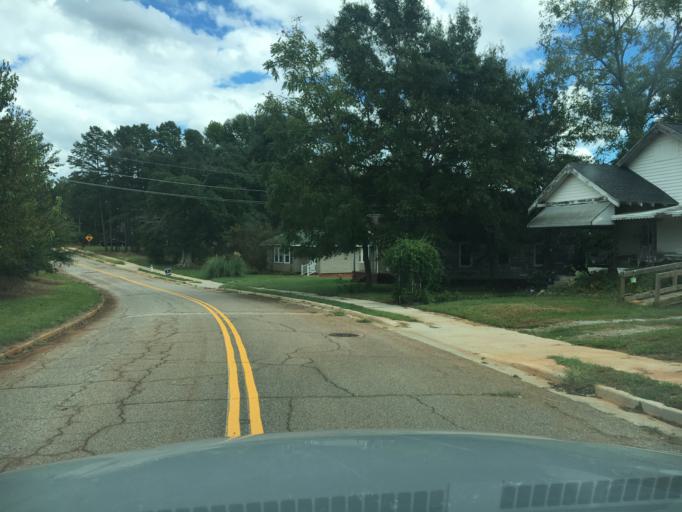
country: US
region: South Carolina
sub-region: Spartanburg County
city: Lyman
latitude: 34.9431
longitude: -82.1255
